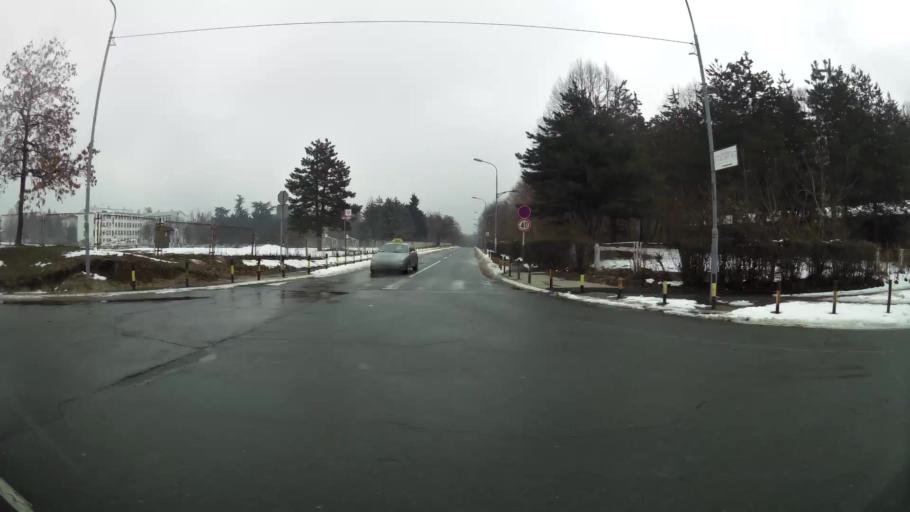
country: RS
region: Central Serbia
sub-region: Belgrade
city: Savski Venac
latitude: 44.7660
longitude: 20.4634
